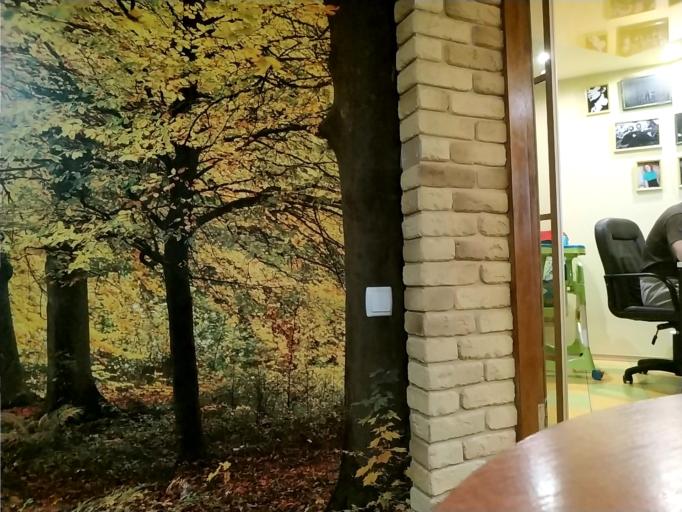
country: RU
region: Tverskaya
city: Staraya Toropa
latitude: 56.3391
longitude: 31.8576
